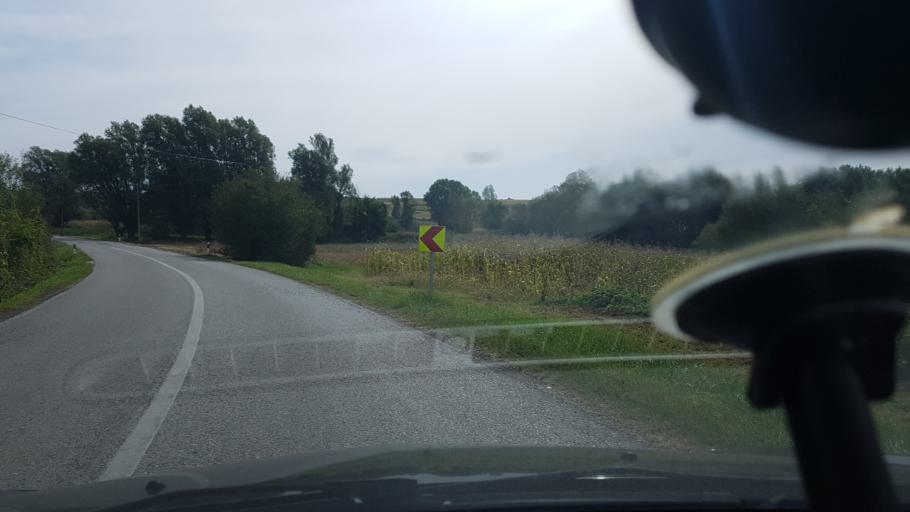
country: HR
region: Varazdinska
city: Ljubescica
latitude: 46.1035
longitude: 16.3934
